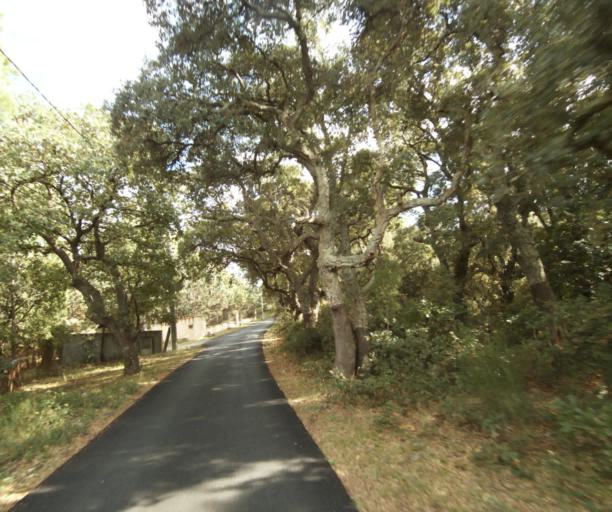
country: FR
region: Languedoc-Roussillon
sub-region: Departement des Pyrenees-Orientales
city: Argelers
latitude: 42.5431
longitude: 2.9994
